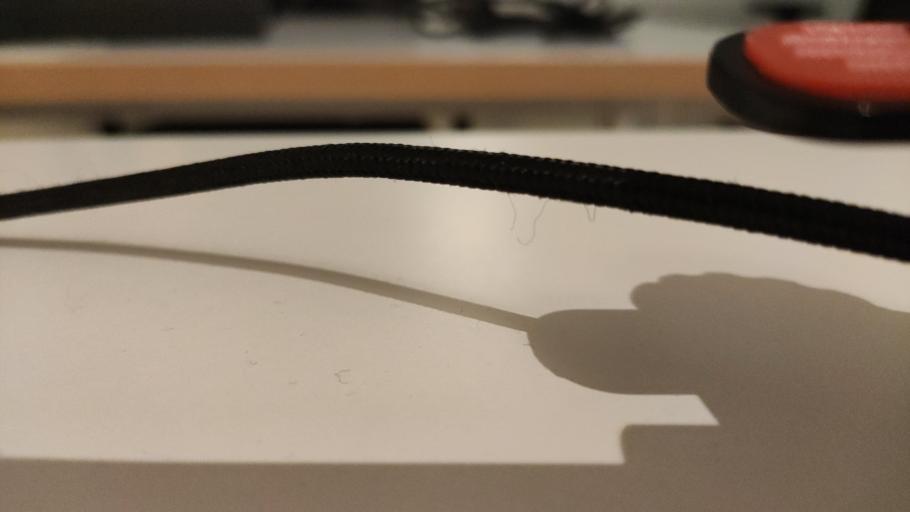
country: RU
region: Moskovskaya
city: Malino
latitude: 55.1102
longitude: 38.1385
